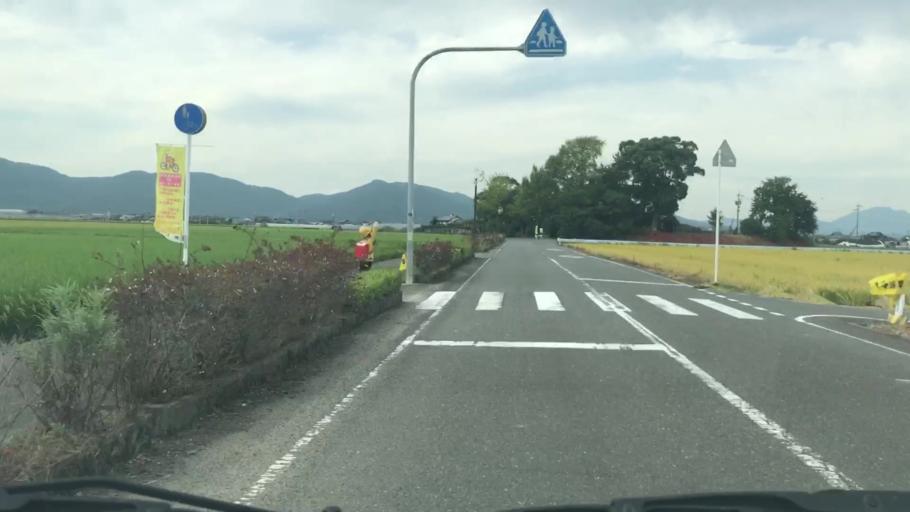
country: JP
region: Saga Prefecture
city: Kashima
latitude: 33.1447
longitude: 130.1447
